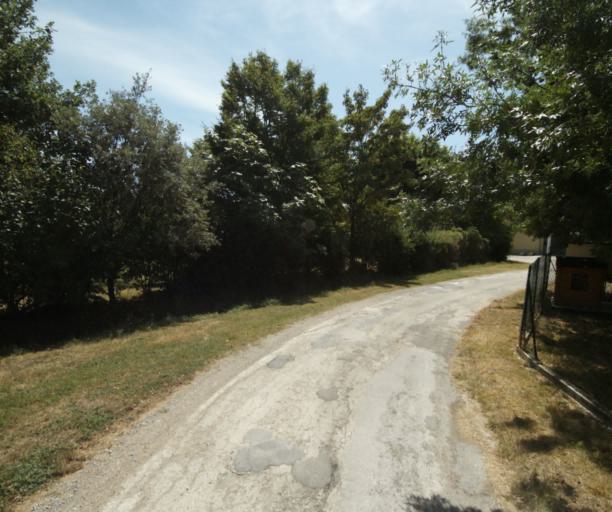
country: FR
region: Midi-Pyrenees
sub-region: Departement de la Haute-Garonne
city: Revel
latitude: 43.4969
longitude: 2.0093
